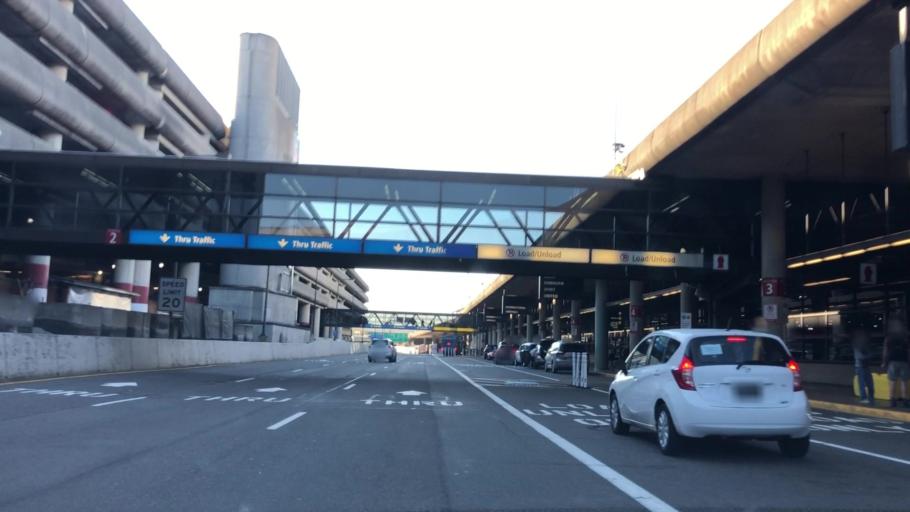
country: US
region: Washington
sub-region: King County
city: SeaTac
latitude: 47.4432
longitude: -122.3012
